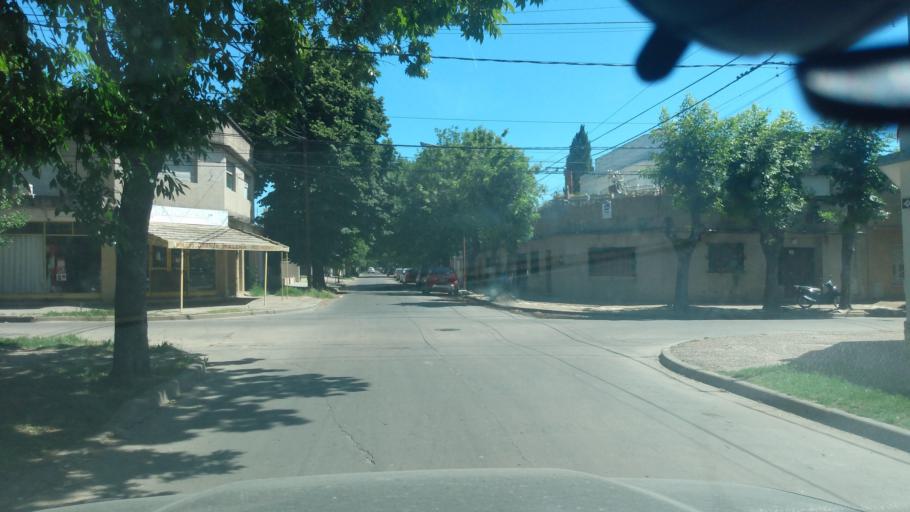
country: AR
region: Buenos Aires
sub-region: Partido de Lujan
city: Lujan
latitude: -34.5671
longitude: -59.1060
